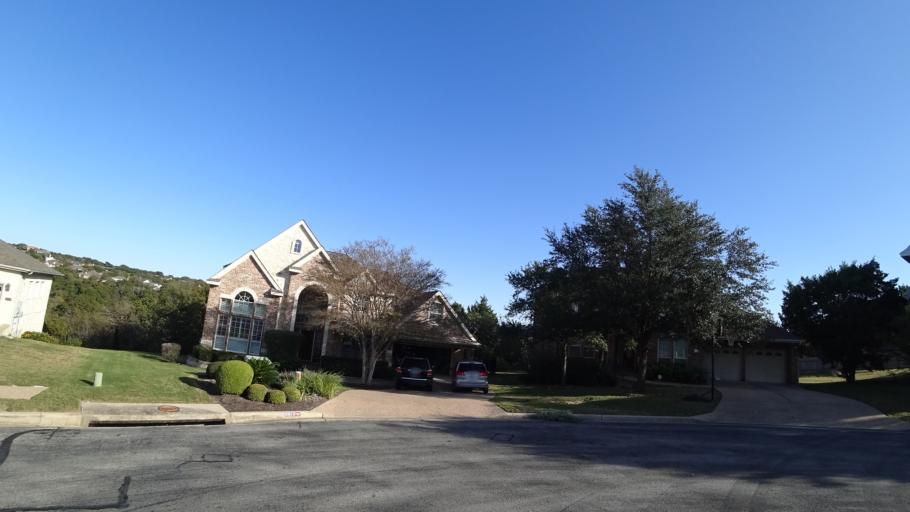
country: US
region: Texas
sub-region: Williamson County
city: Jollyville
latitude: 30.4067
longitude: -97.7758
